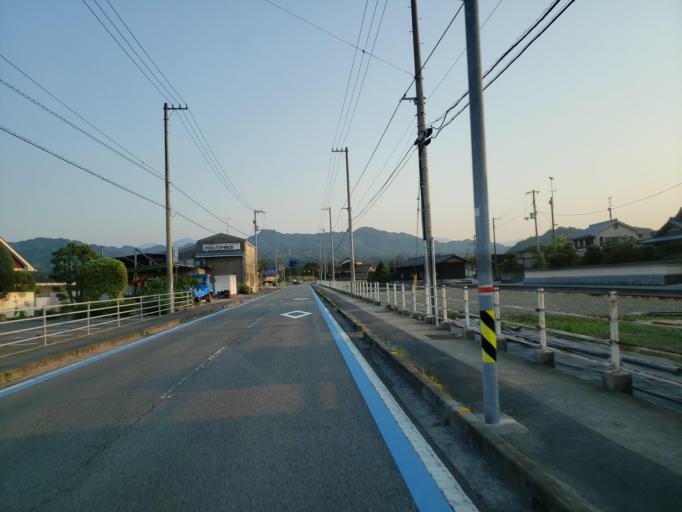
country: JP
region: Ehime
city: Hojo
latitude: 34.0367
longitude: 132.9725
